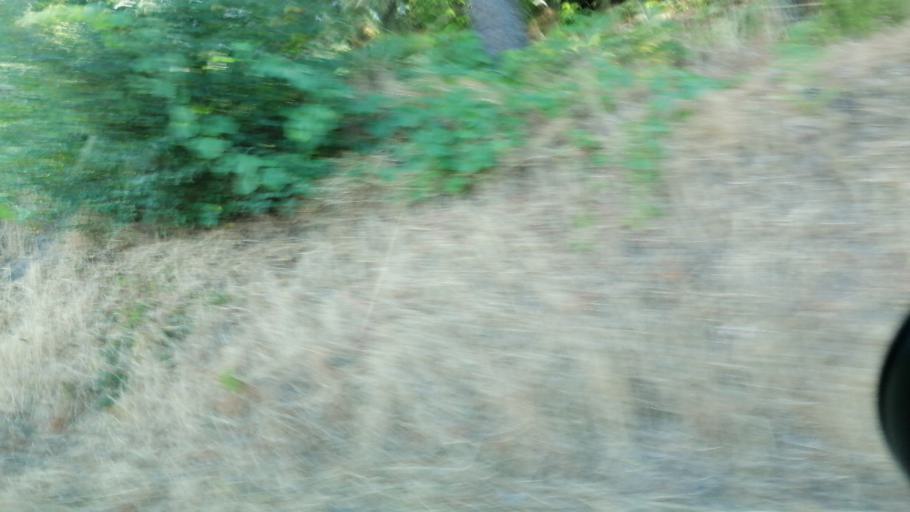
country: PT
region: Vila Real
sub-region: Murca
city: Murca
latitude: 41.3772
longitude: -7.5461
